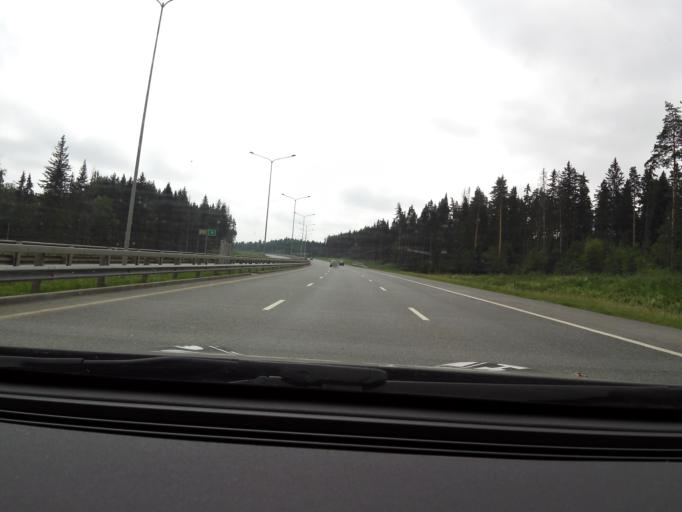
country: RU
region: Perm
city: Lobanovo
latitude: 57.8584
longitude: 56.2605
